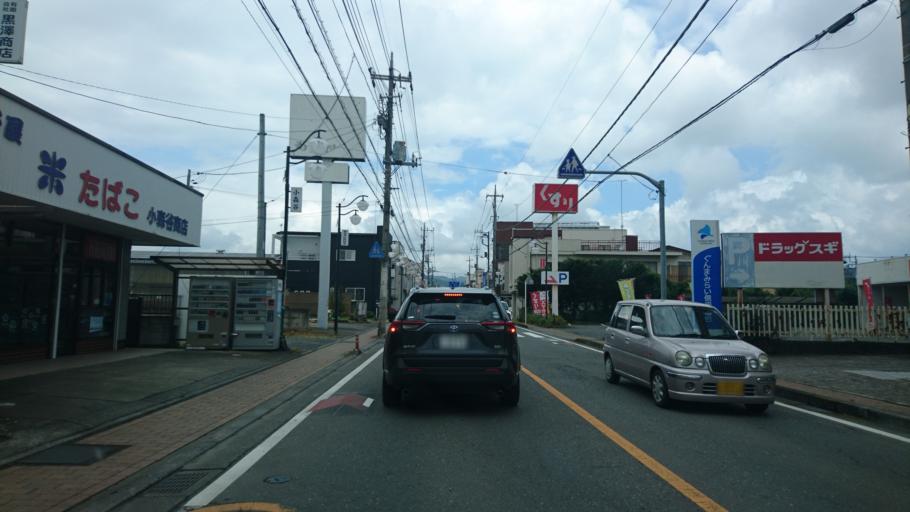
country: JP
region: Gunma
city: Omamacho-omama
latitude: 36.4274
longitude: 139.2756
